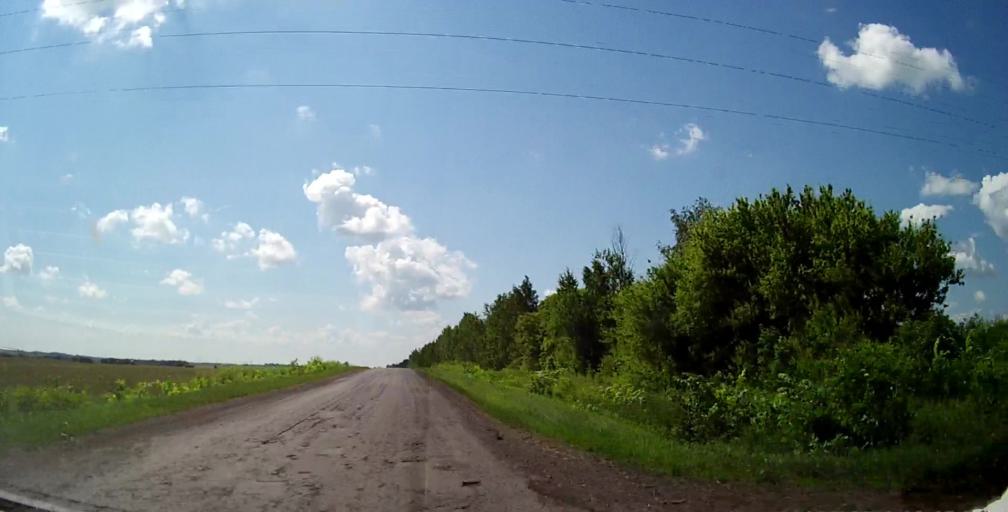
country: RU
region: Lipetsk
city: Chaplygin
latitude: 53.2922
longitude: 39.9569
